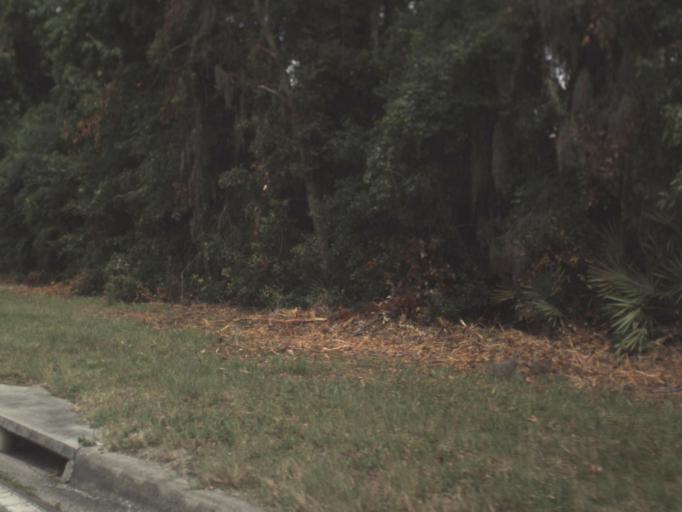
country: US
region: Florida
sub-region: Duval County
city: Jacksonville
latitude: 30.4076
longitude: -81.6307
